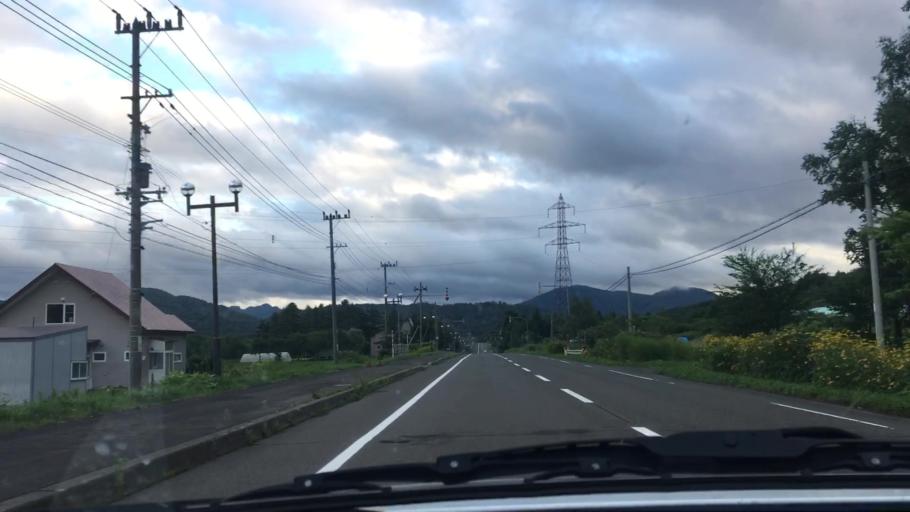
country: JP
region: Hokkaido
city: Shimo-furano
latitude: 42.9987
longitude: 142.4048
